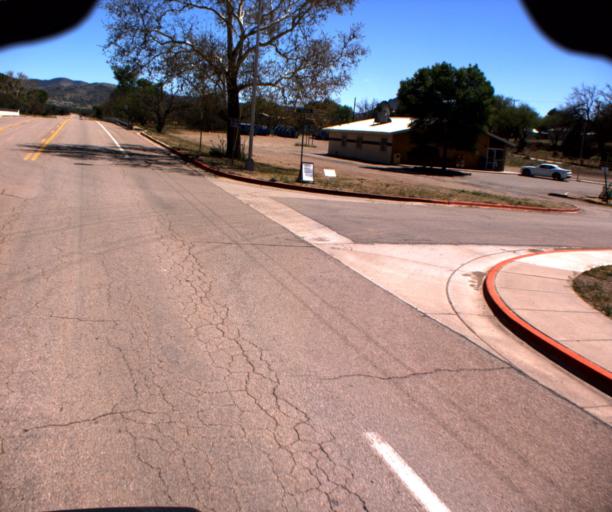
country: US
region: Arizona
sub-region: Santa Cruz County
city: Rio Rico
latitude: 31.5416
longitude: -110.7521
